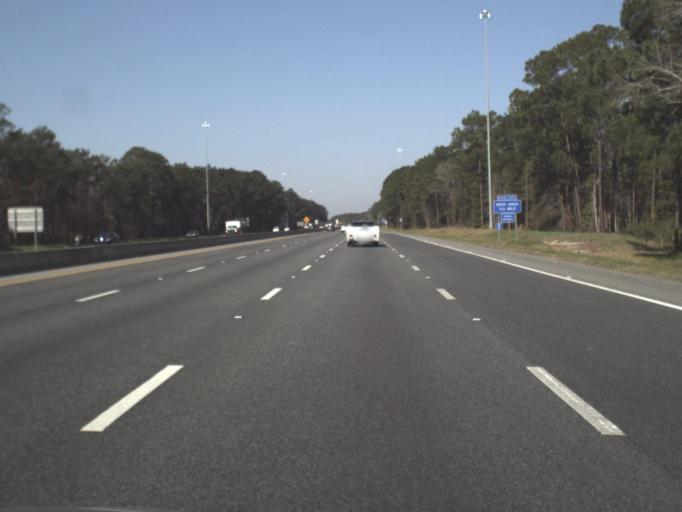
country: US
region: Florida
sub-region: Gadsden County
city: Midway
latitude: 30.4813
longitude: -84.3703
